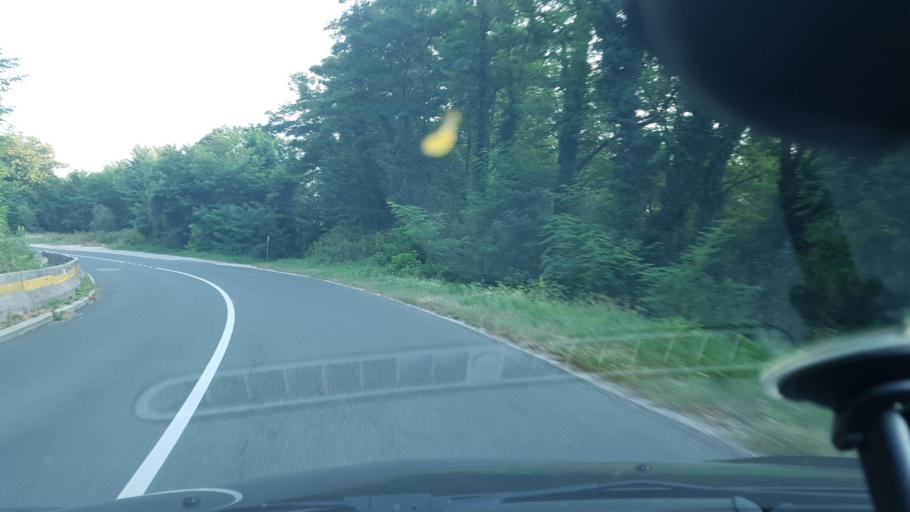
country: HR
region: Krapinsko-Zagorska
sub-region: Grad Krapina
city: Krapina
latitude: 46.1672
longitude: 15.8510
